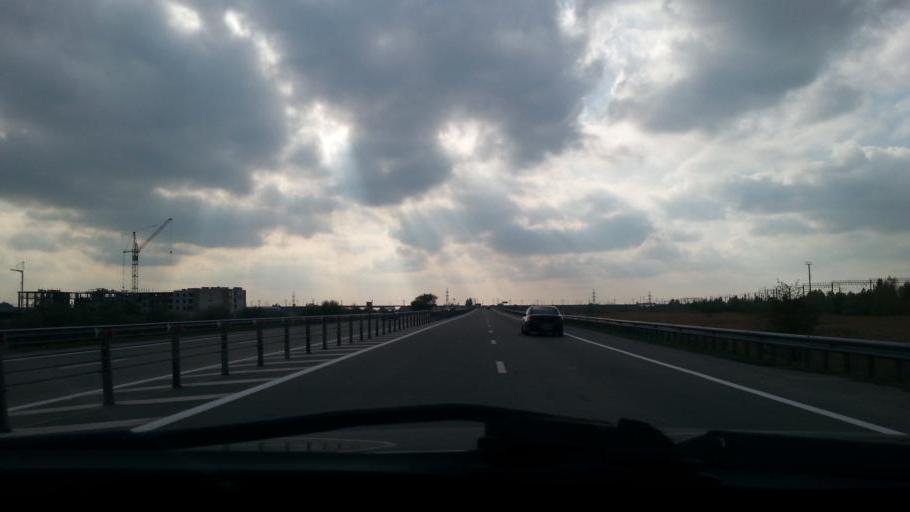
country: RU
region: Rostov
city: Bataysk
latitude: 47.1504
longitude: 39.7109
